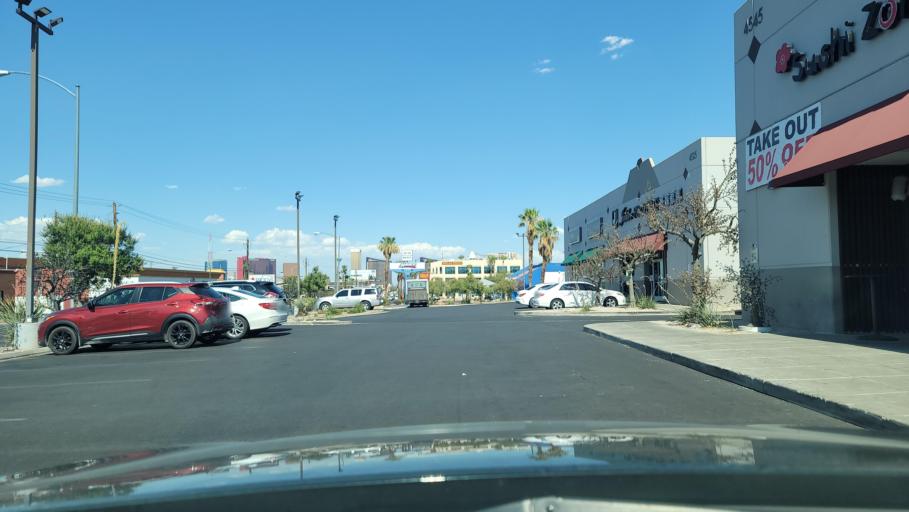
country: US
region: Nevada
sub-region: Clark County
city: Spring Valley
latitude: 36.1260
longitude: -115.2025
